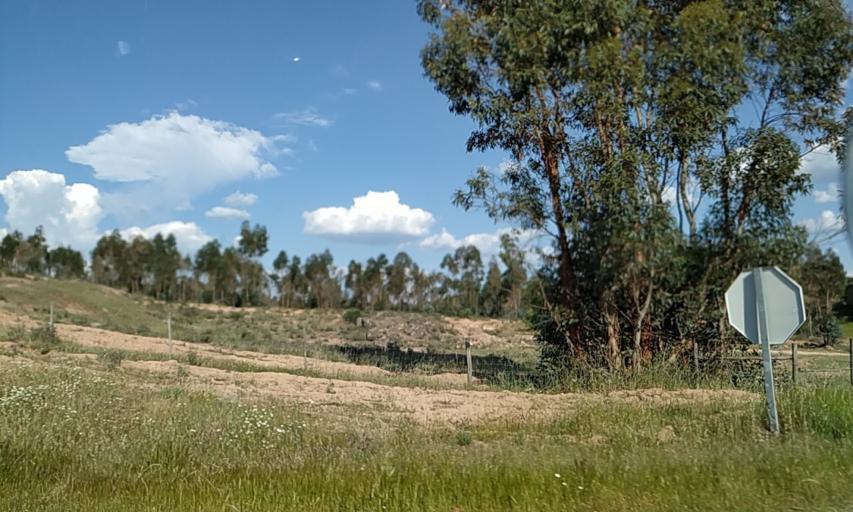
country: PT
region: Portalegre
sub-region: Fronteira
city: Fronteira
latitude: 38.9970
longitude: -7.4705
